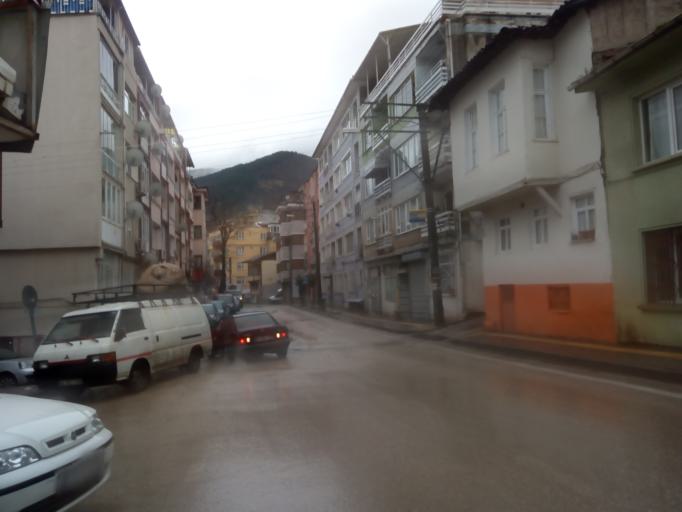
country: TR
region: Bursa
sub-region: Osmangazi
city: Bursa
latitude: 40.1790
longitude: 29.0591
